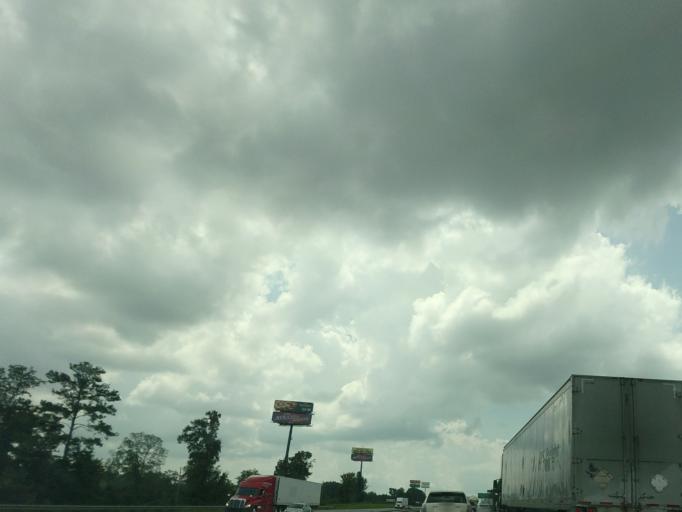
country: US
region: Georgia
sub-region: Peach County
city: Byron
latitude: 32.6091
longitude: -83.7427
